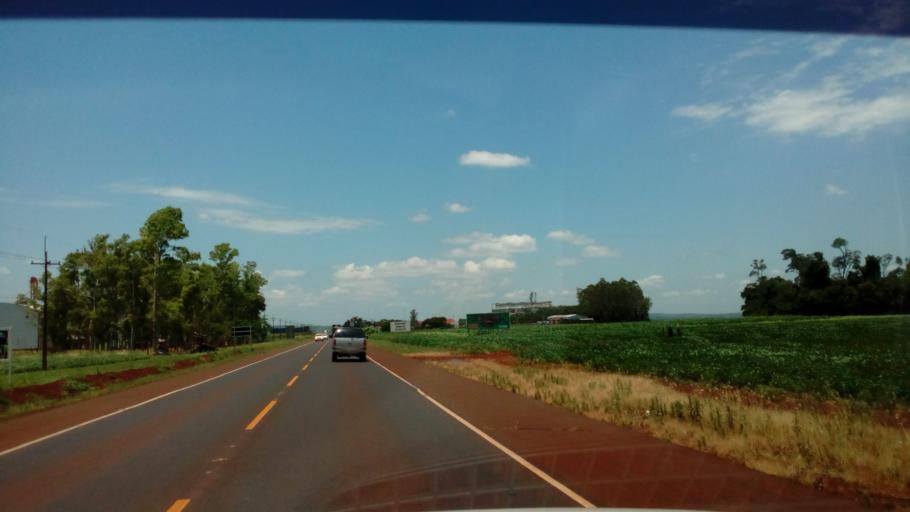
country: PY
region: Alto Parana
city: Santa Rita
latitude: -25.8756
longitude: -55.1190
